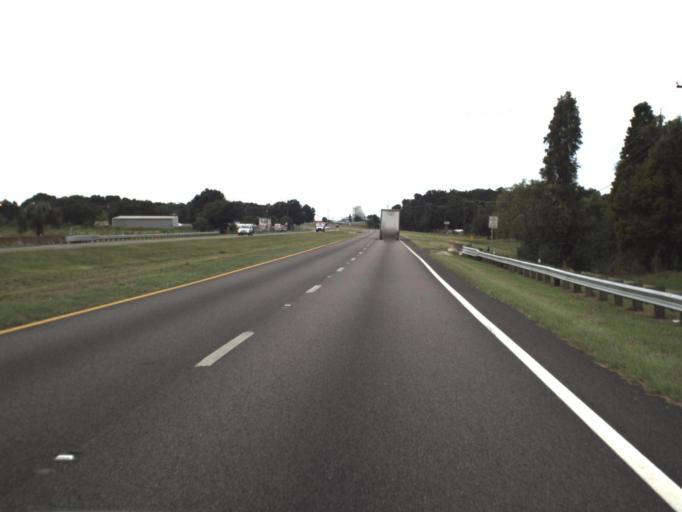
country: US
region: Florida
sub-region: Polk County
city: Bartow
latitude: 27.8645
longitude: -81.8288
